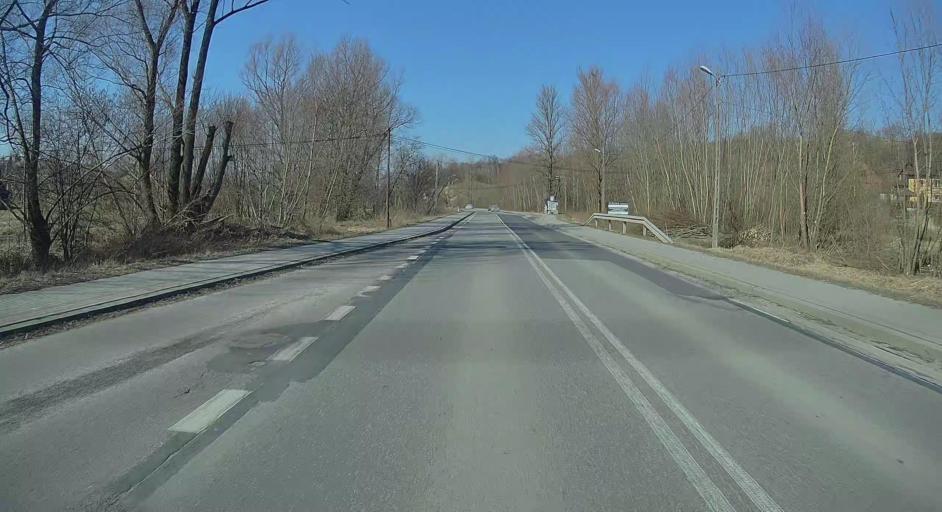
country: PL
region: Subcarpathian Voivodeship
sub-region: Powiat rzeszowski
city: Hyzne
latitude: 49.9170
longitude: 22.1812
